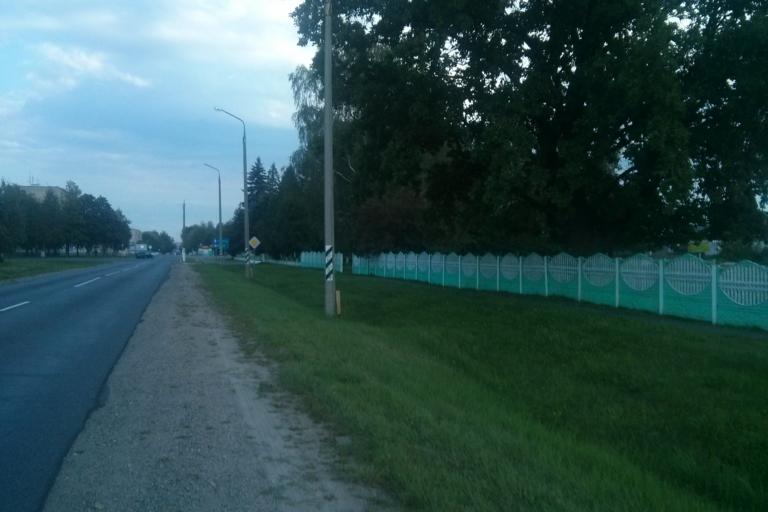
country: BY
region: Minsk
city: Chervyen'
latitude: 53.7200
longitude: 28.3949
